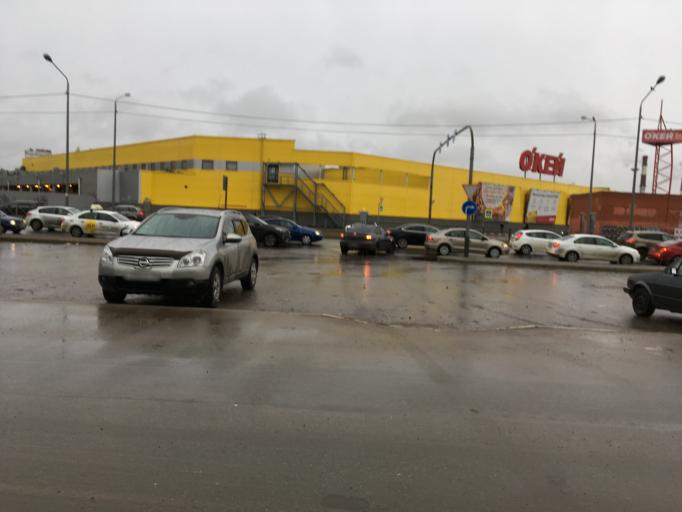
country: RU
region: St.-Petersburg
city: Komendantsky aerodrom
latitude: 60.0006
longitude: 30.2691
